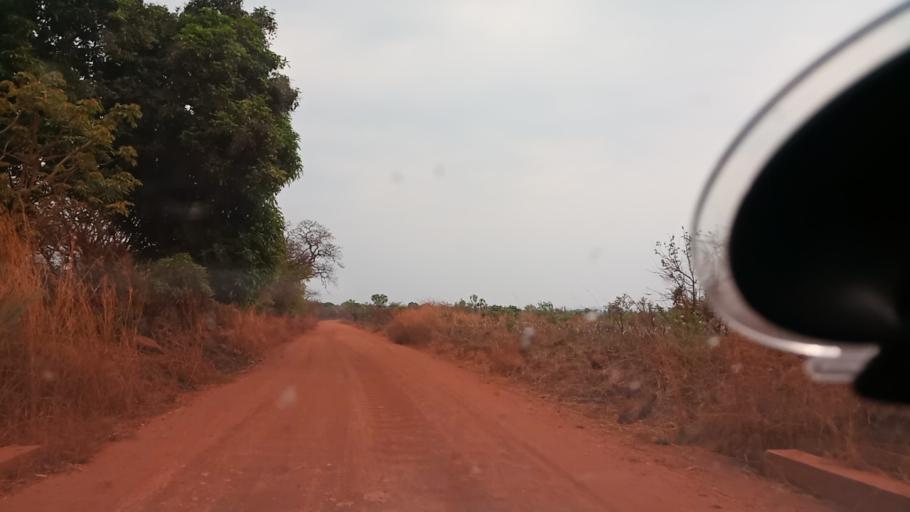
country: ZM
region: Luapula
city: Nchelenge
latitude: -9.1744
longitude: 28.2816
